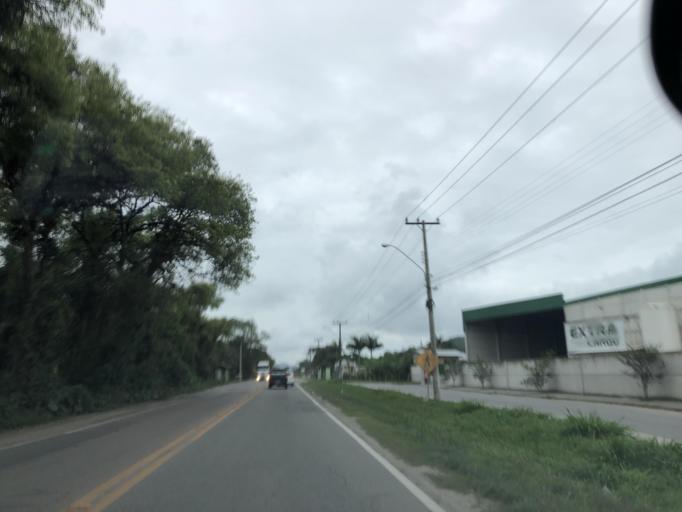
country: BR
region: Santa Catarina
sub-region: Sao Francisco Do Sul
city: Sao Francisco do Sul
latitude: -26.2484
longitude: -48.6065
